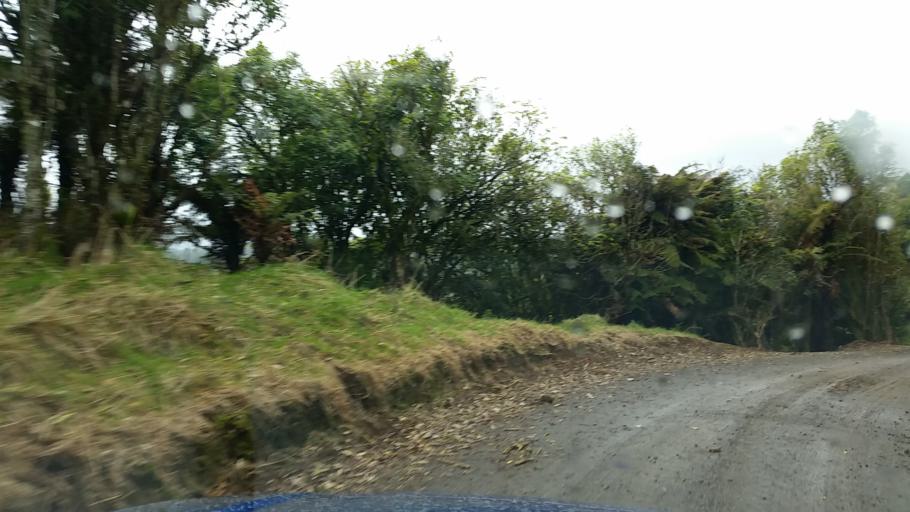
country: NZ
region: Taranaki
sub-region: South Taranaki District
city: Eltham
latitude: -39.1674
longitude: 174.6283
